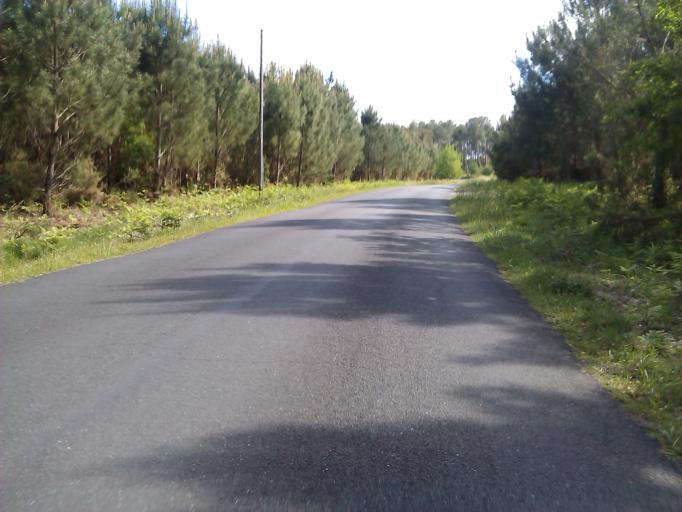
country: FR
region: Aquitaine
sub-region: Departement des Landes
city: Leon
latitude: 43.8618
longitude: -1.3569
